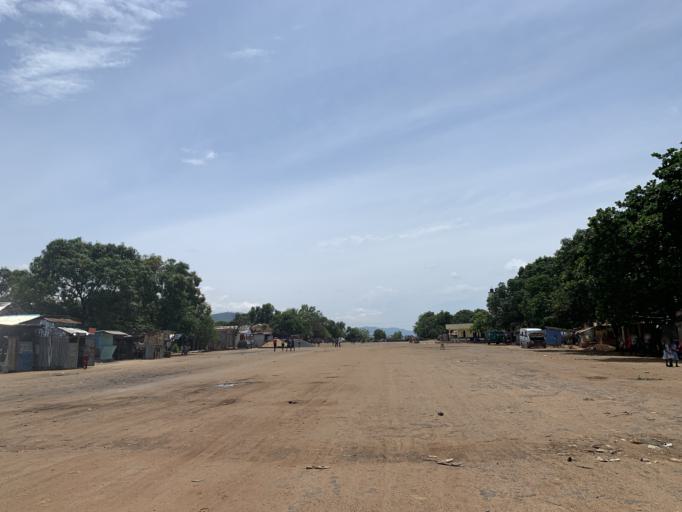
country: SL
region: Western Area
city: Waterloo
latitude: 8.3400
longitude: -13.0473
